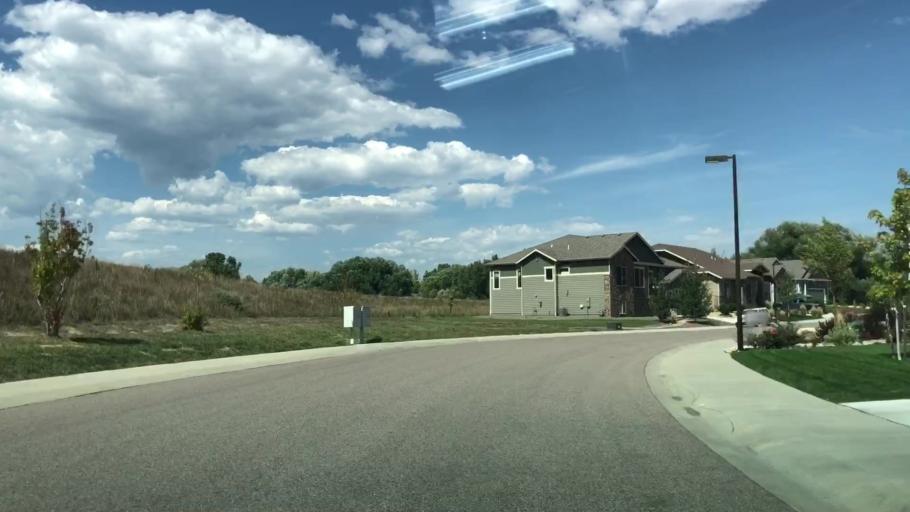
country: US
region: Colorado
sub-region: Larimer County
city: Loveland
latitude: 40.3950
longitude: -105.1583
